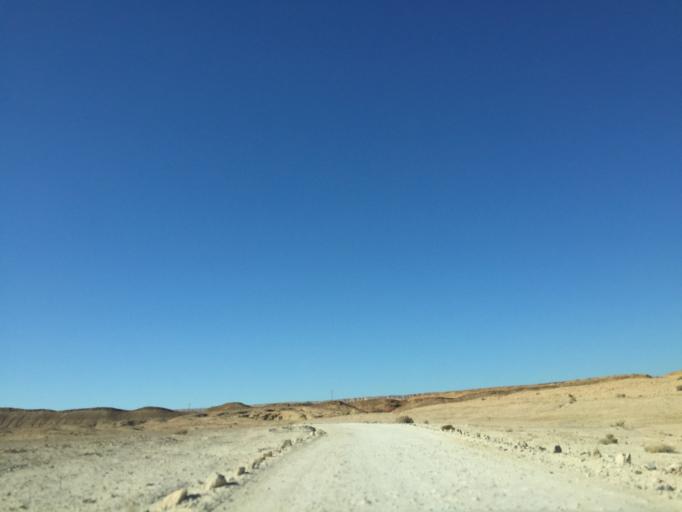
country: IL
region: Southern District
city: Mitzpe Ramon
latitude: 30.6141
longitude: 34.9073
